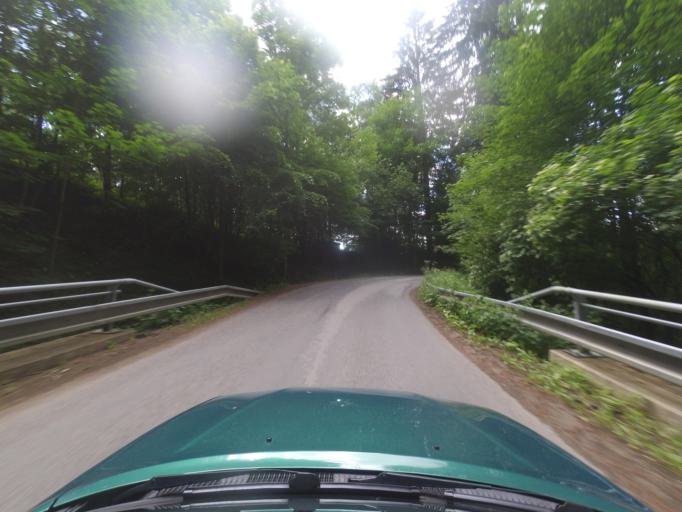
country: CZ
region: Pardubicky
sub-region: Okres Usti nad Orlici
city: Kunvald
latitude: 50.1138
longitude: 16.5570
